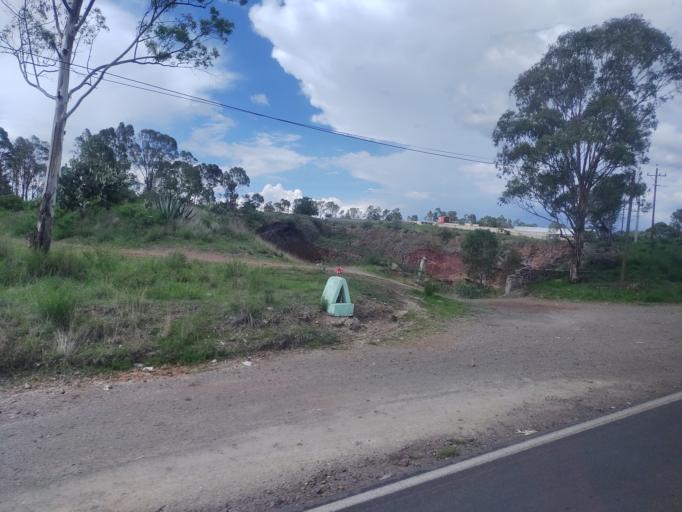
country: MX
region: Mexico
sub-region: Aculco
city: El Colorado
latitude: 20.0911
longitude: -99.7752
